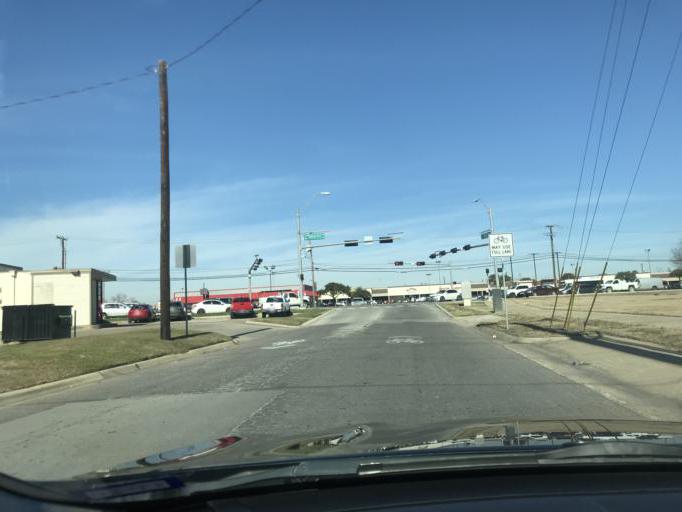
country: US
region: Texas
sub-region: Denton County
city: Denton
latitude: 33.2298
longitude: -97.1400
